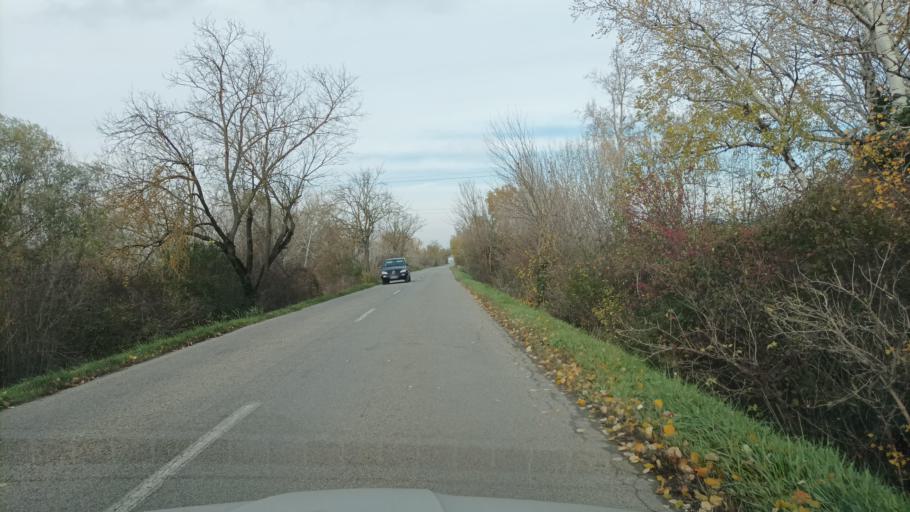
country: HU
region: Fejer
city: Adony
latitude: 47.0966
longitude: 18.9274
